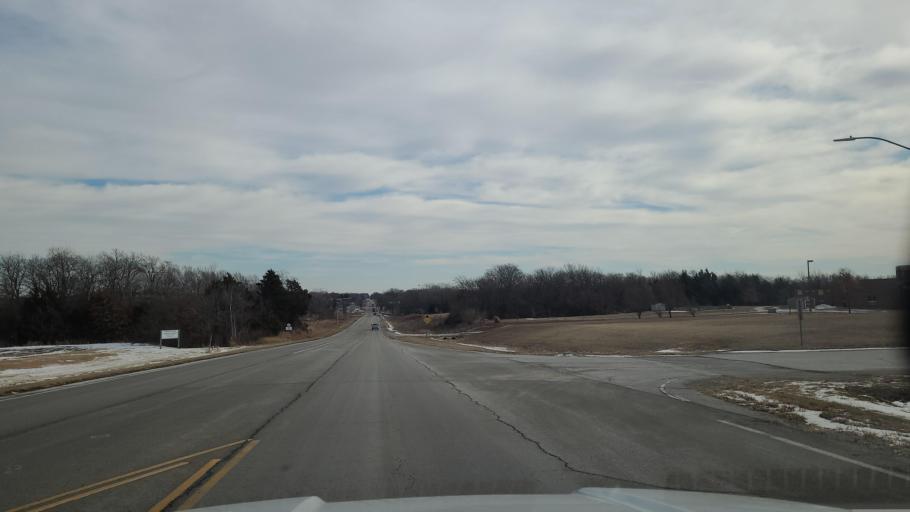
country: US
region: Kansas
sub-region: Douglas County
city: Baldwin City
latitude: 38.7821
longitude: -95.2000
